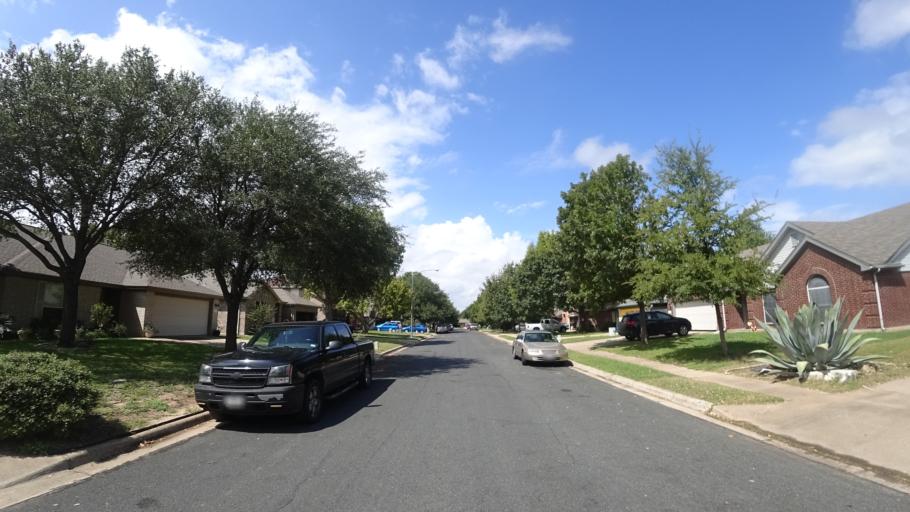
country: US
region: Texas
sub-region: Travis County
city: Onion Creek
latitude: 30.1651
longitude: -97.7388
